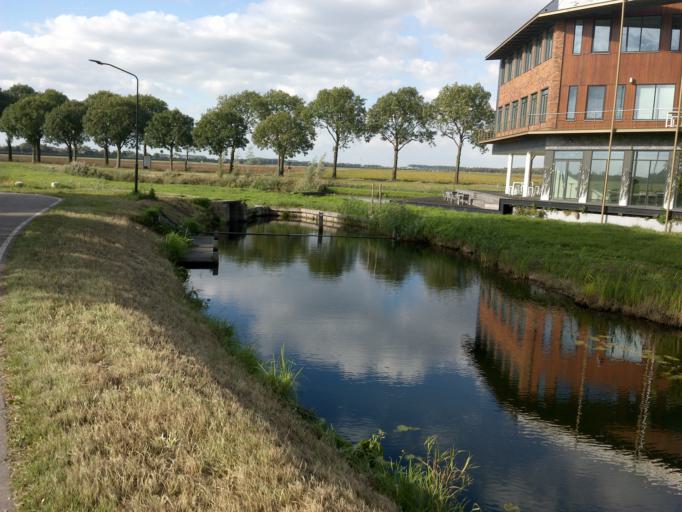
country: NL
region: North Brabant
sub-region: Gemeente Woudrichem
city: Almkerk
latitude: 51.7704
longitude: 4.9394
